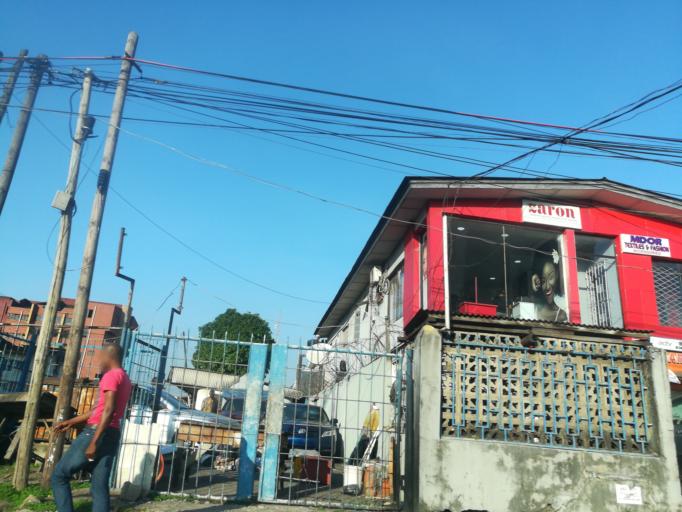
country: NG
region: Lagos
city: Ikeja
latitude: 6.6010
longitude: 3.3524
